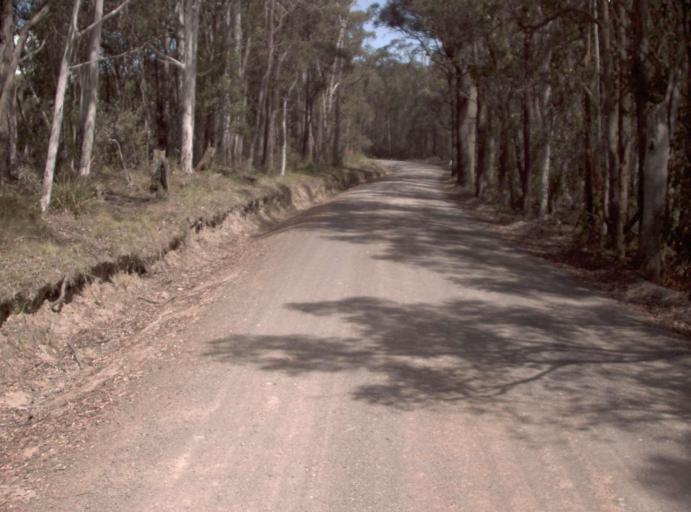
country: AU
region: New South Wales
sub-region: Bombala
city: Bombala
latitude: -37.1781
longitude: 148.6970
